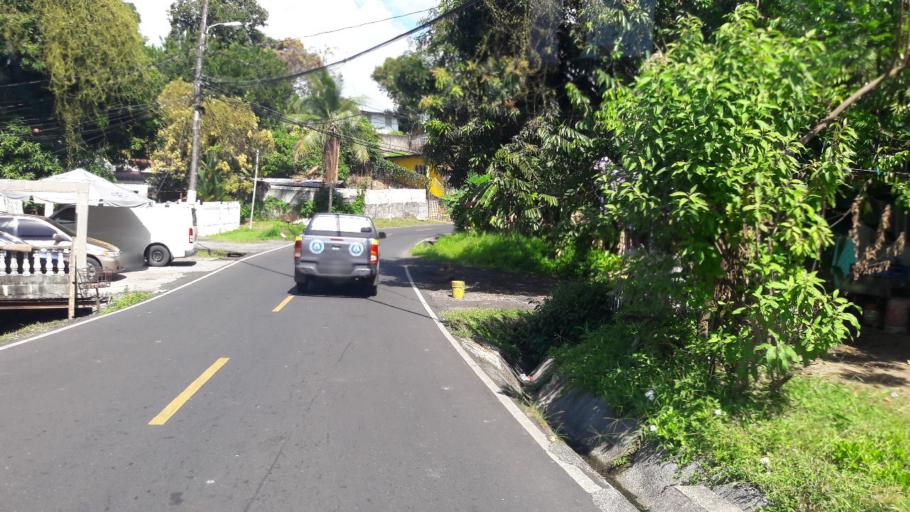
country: PA
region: Panama
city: San Miguelito
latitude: 9.0464
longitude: -79.5040
